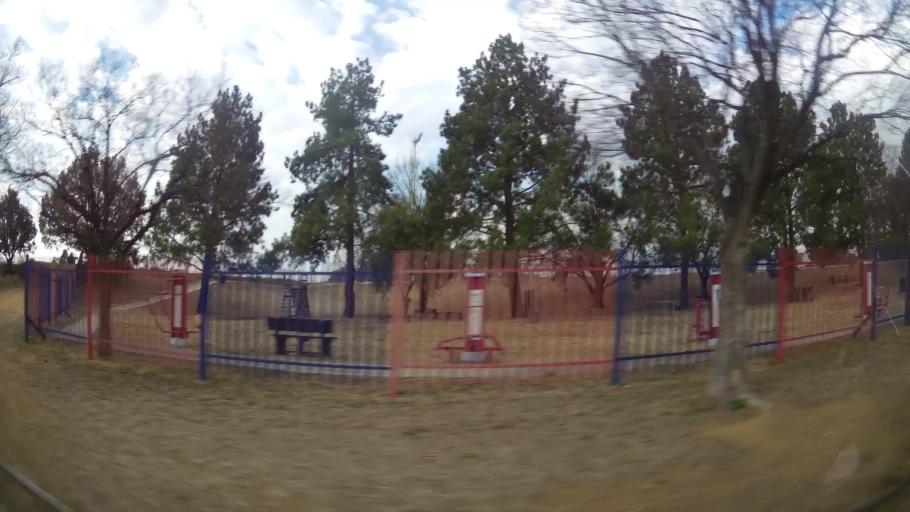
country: ZA
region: Orange Free State
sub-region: Fezile Dabi District Municipality
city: Sasolburg
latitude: -26.7928
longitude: 27.8237
